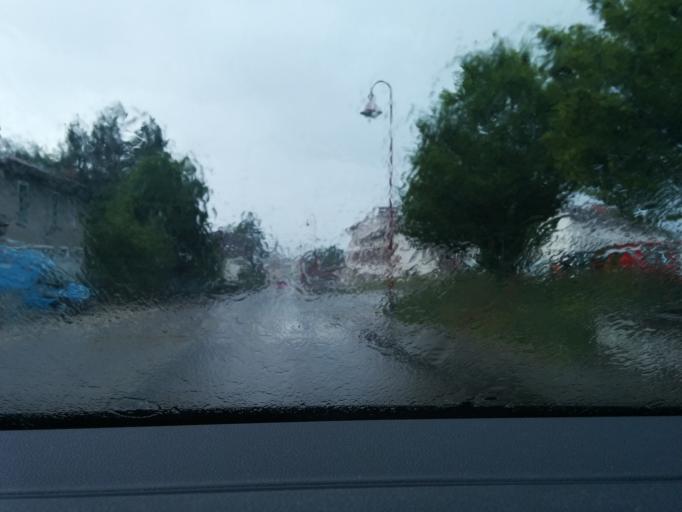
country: FR
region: Franche-Comte
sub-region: Departement du Jura
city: Saint-Lupicin
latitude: 46.4053
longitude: 5.7940
